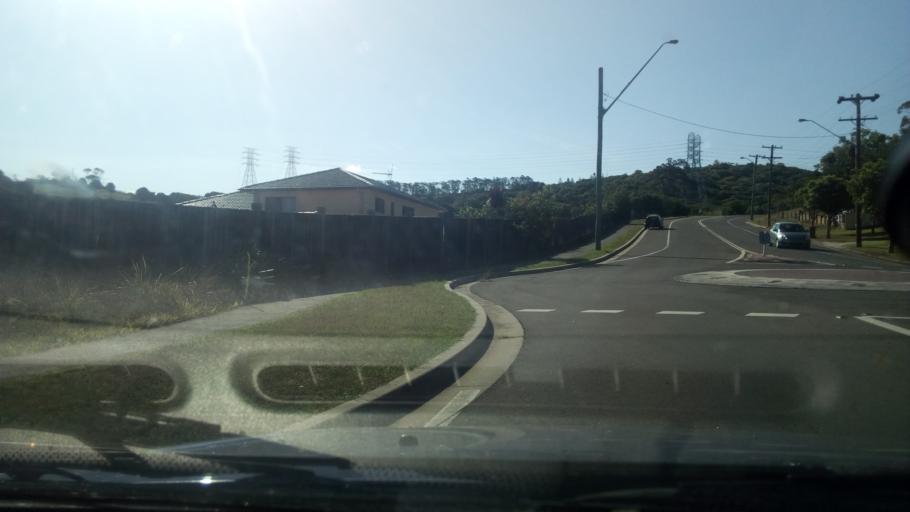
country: AU
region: New South Wales
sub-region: Wollongong
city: Berkeley
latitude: -34.4728
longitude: 150.8535
